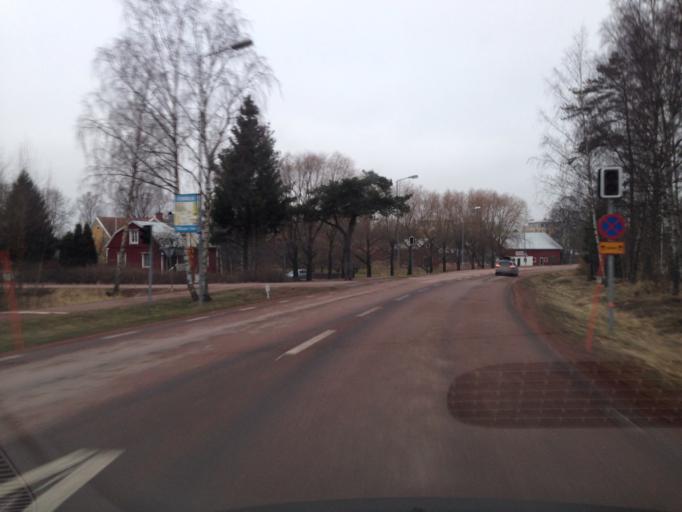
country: AX
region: Mariehamns stad
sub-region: Mariehamn
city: Mariehamn
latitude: 60.1072
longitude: 19.9316
